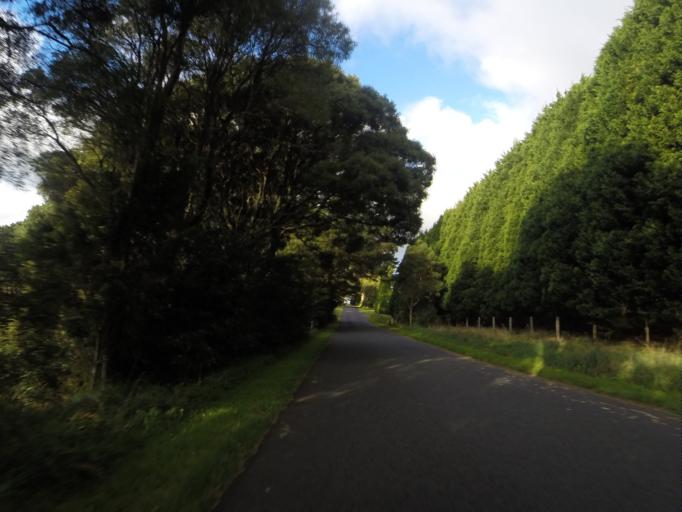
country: AU
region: New South Wales
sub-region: Shoalhaven Shire
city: Kangaroo Valley
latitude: -34.6014
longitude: 150.5525
